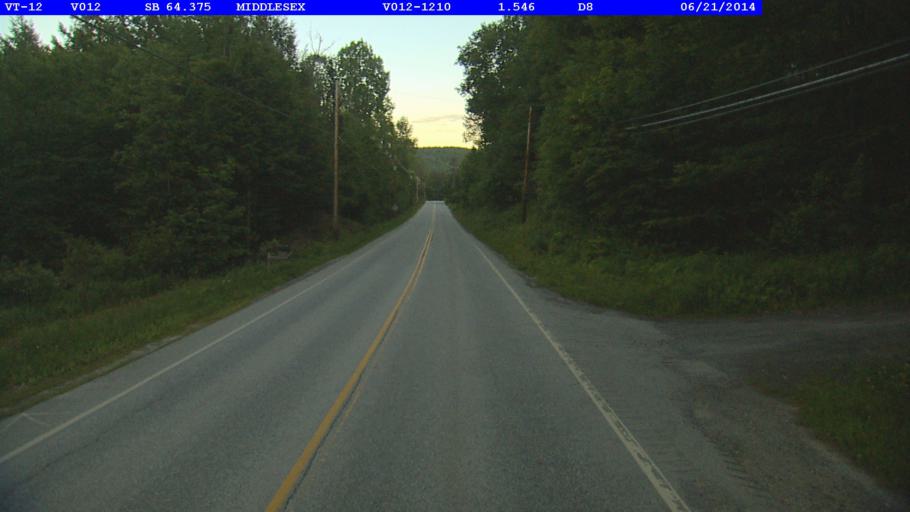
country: US
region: Vermont
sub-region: Washington County
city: Montpelier
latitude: 44.3269
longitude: -72.5801
